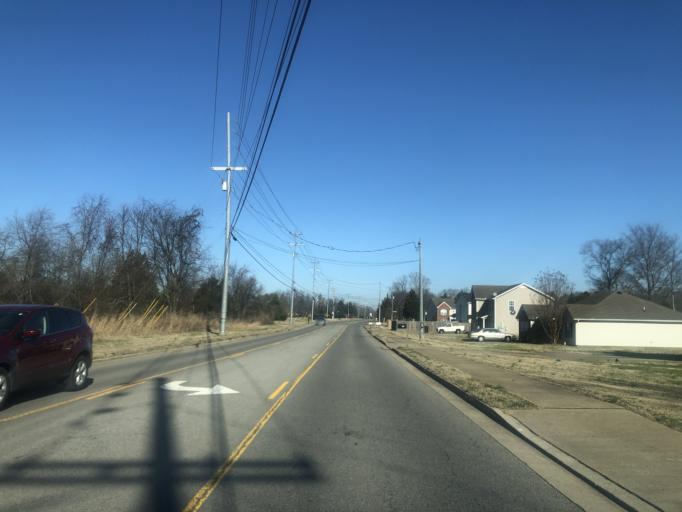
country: US
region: Tennessee
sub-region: Rutherford County
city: Smyrna
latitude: 35.9077
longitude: -86.4733
